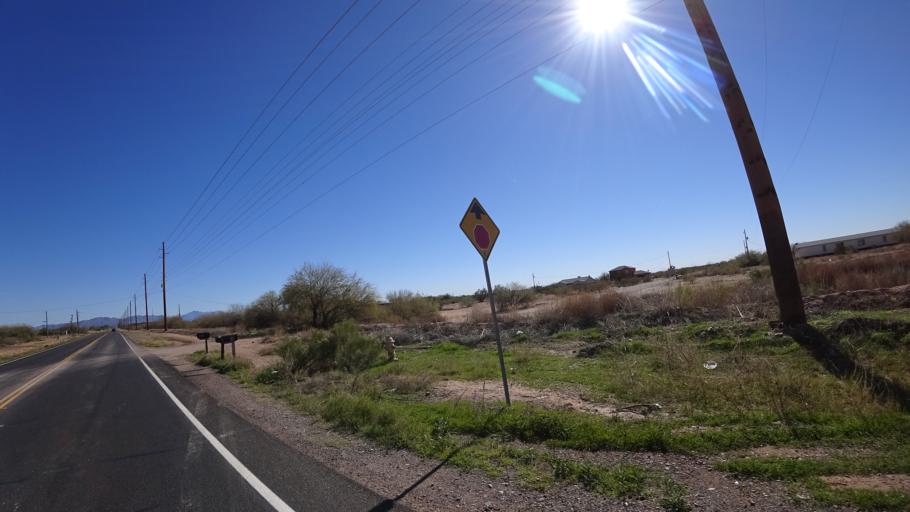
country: US
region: Arizona
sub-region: Maricopa County
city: Scottsdale
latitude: 33.4951
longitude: -111.8417
